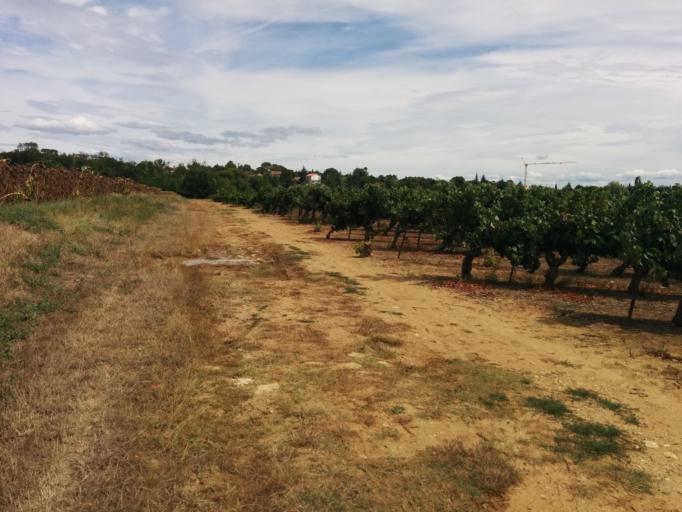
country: FR
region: Languedoc-Roussillon
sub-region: Departement du Gard
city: Saint-Christol-les-Ales
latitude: 44.0906
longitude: 4.0745
